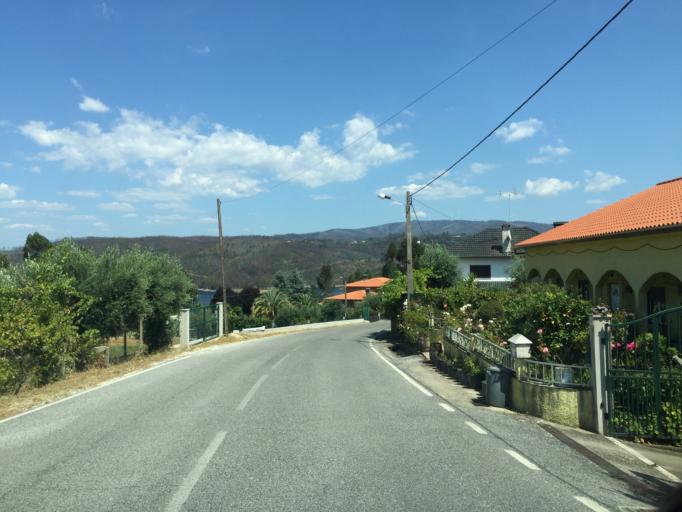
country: PT
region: Leiria
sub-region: Pedrogao Grande
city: Pedrogao Grande
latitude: 39.9247
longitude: -8.1352
